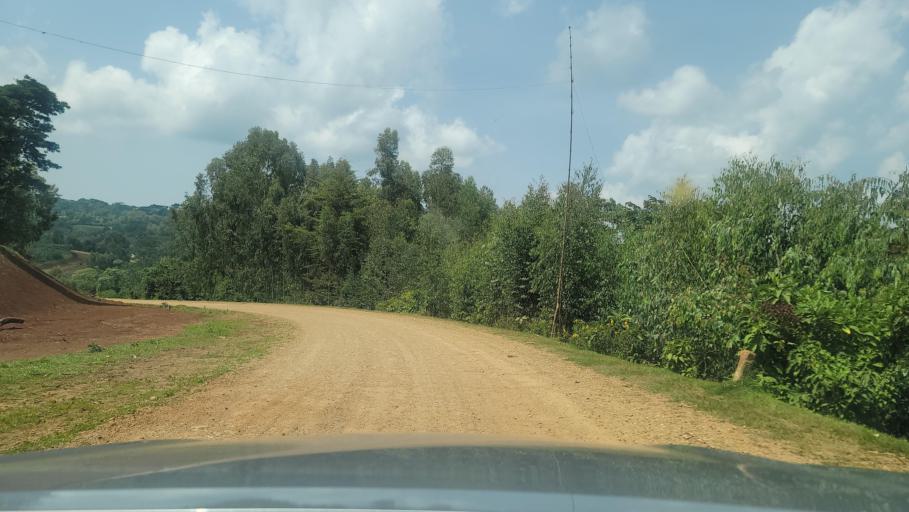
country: ET
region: Oromiya
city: Agaro
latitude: 7.7929
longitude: 36.4538
